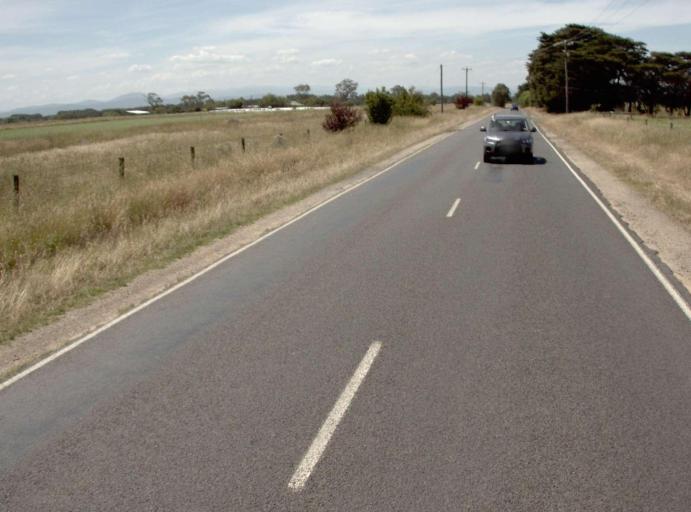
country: AU
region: Victoria
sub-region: Wellington
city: Heyfield
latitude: -38.0210
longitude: 146.8813
